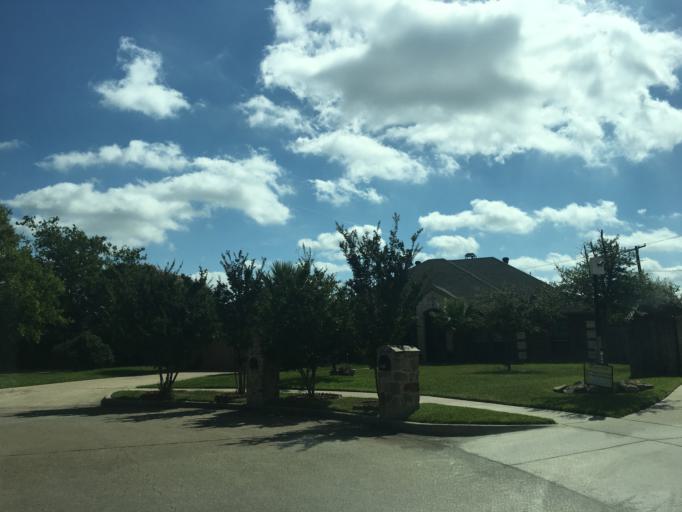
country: US
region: Texas
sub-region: Dallas County
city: Garland
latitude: 32.8488
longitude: -96.6603
